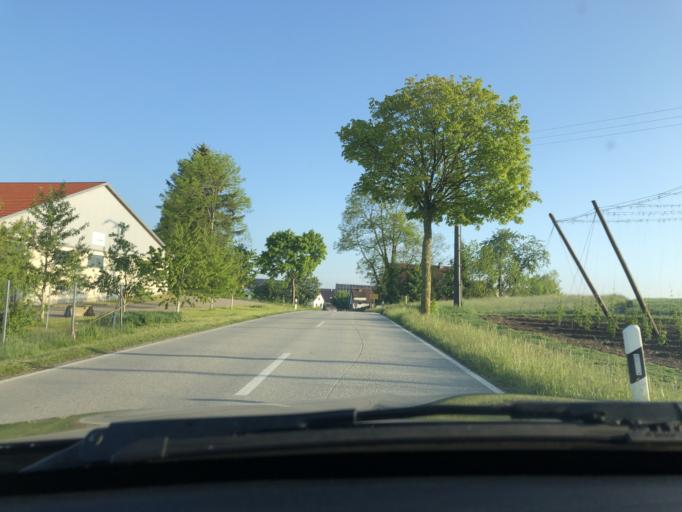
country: DE
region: Bavaria
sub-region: Upper Bavaria
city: Schweitenkirchen
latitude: 48.4842
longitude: 11.6291
